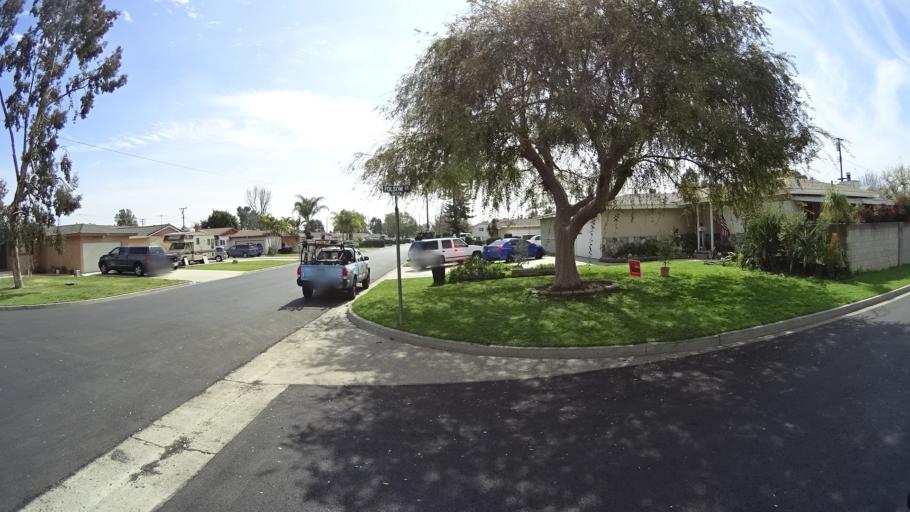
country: US
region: California
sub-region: Orange County
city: Garden Grove
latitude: 33.8063
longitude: -117.9514
